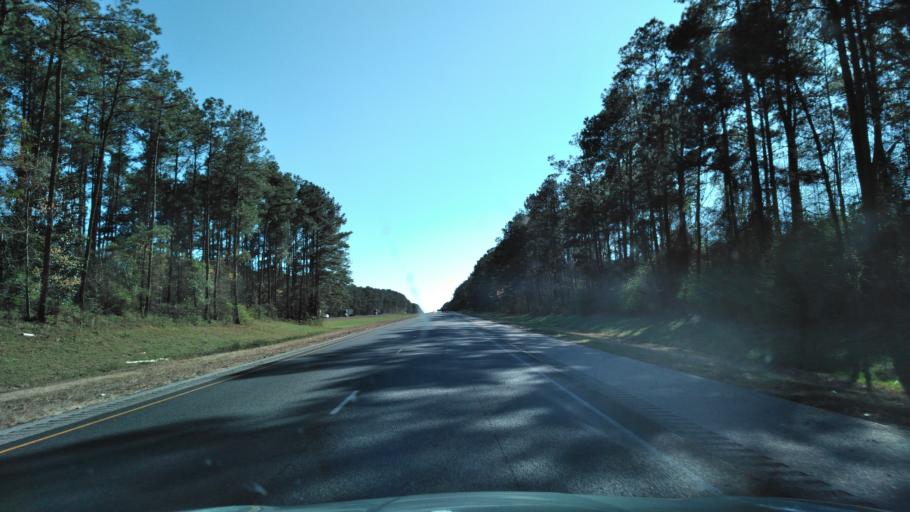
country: US
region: Alabama
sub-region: Butler County
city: Georgiana
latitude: 31.6939
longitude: -86.7459
